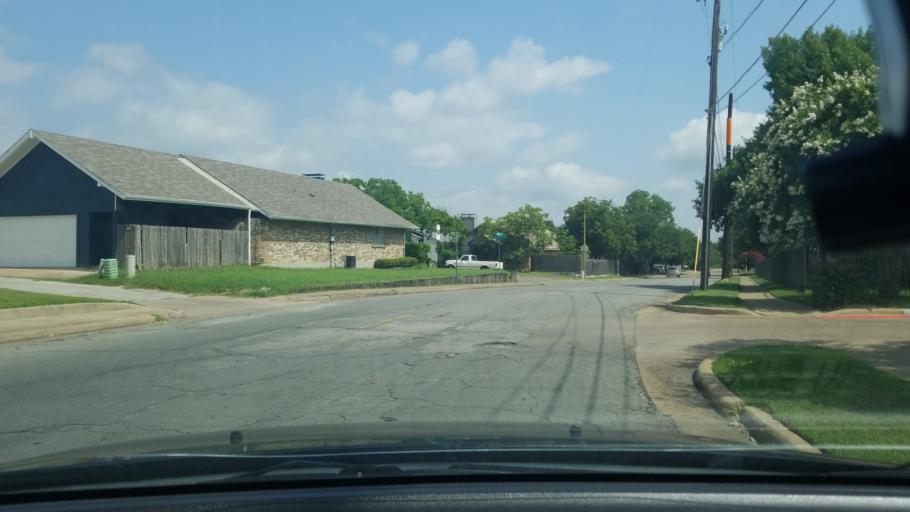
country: US
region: Texas
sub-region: Dallas County
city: Mesquite
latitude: 32.8078
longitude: -96.6893
